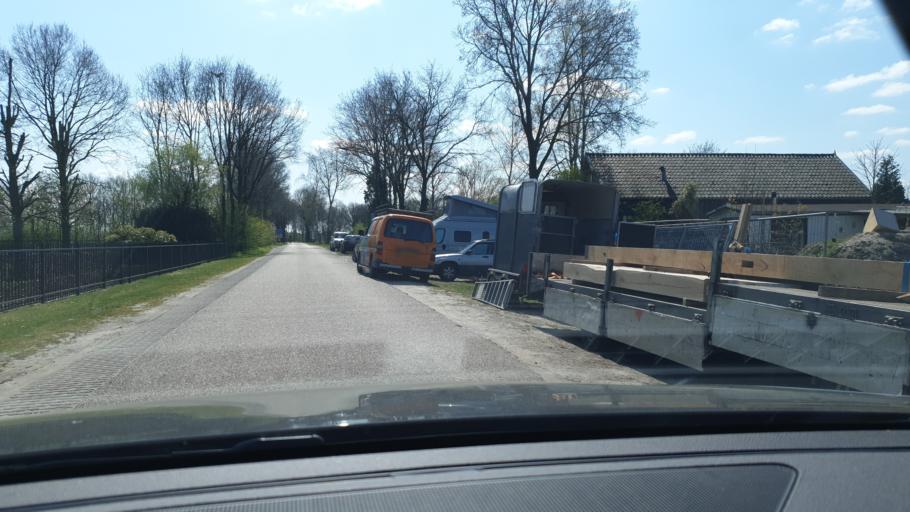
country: NL
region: North Brabant
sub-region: Gemeente Bladel en Netersel
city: Bladel
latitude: 51.3929
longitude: 5.2432
